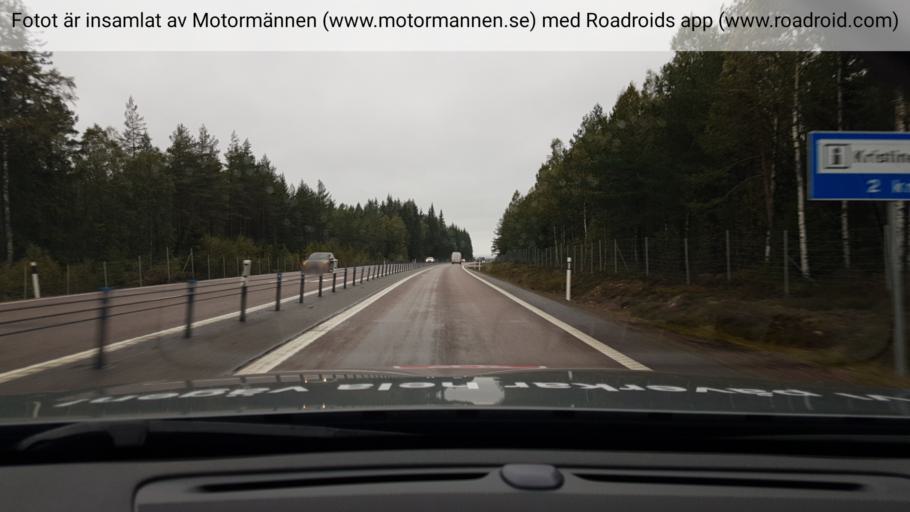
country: SE
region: Vaermland
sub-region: Kristinehamns Kommun
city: Bjorneborg
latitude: 59.3120
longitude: 14.2346
